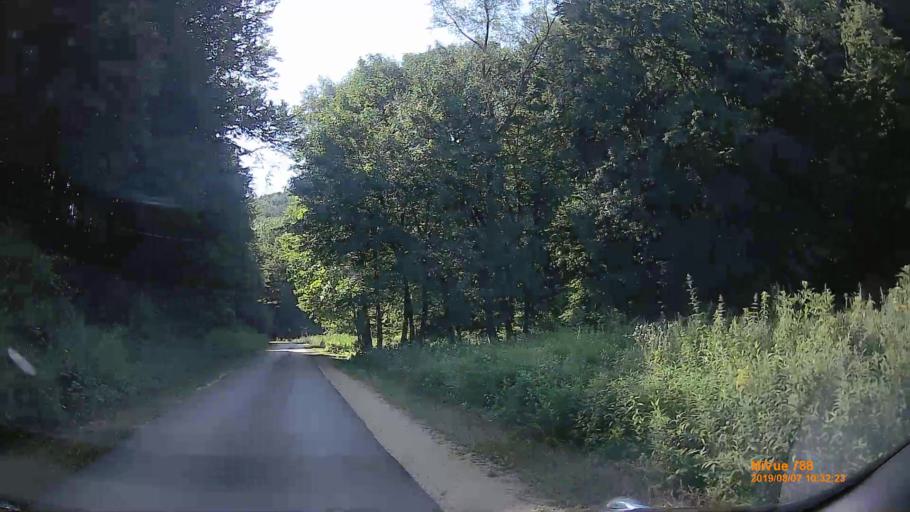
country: HU
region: Veszprem
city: Ajka
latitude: 47.0676
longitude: 17.5872
